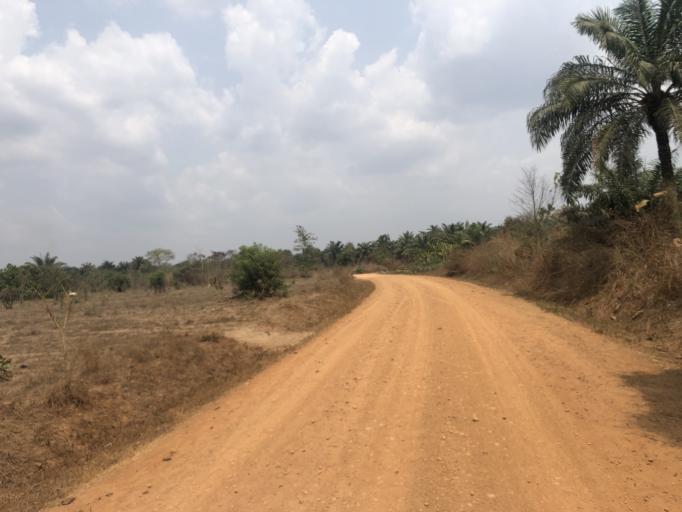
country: NG
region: Osun
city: Bode Osi
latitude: 7.7566
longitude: 4.2444
